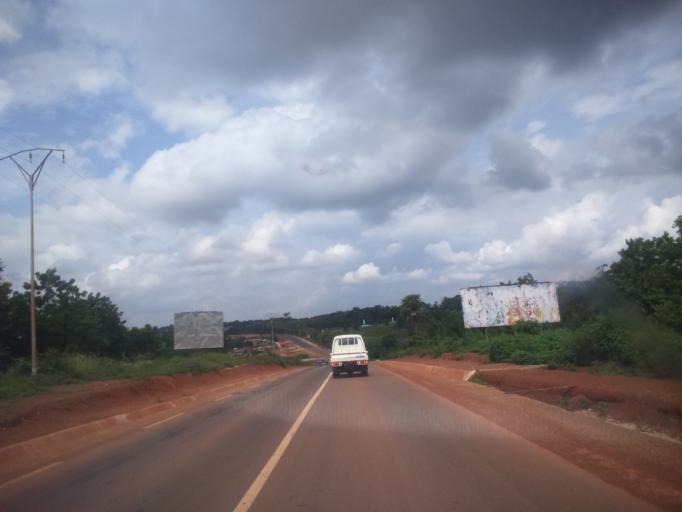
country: CI
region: Moyen-Comoe
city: Abengourou
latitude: 6.7210
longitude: -3.5258
